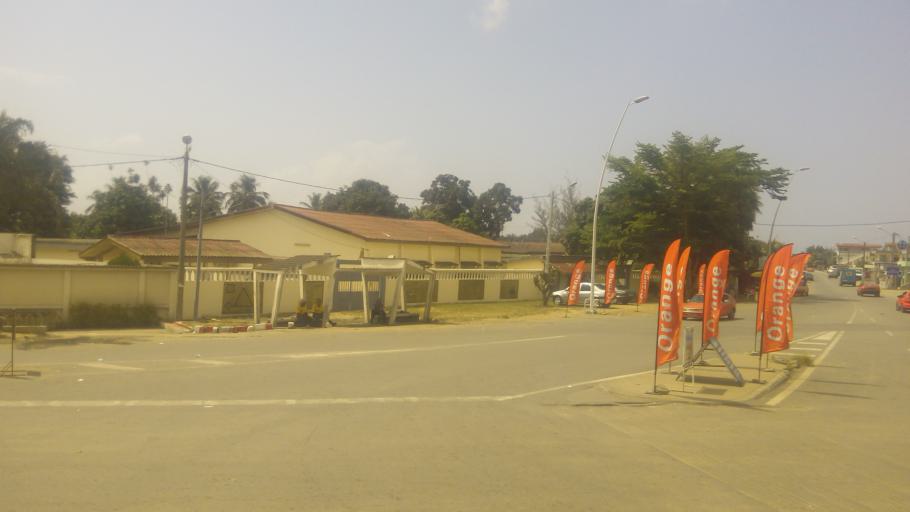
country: CI
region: Sud-Comoe
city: Grand-Bassam
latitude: 5.2221
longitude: -3.7250
